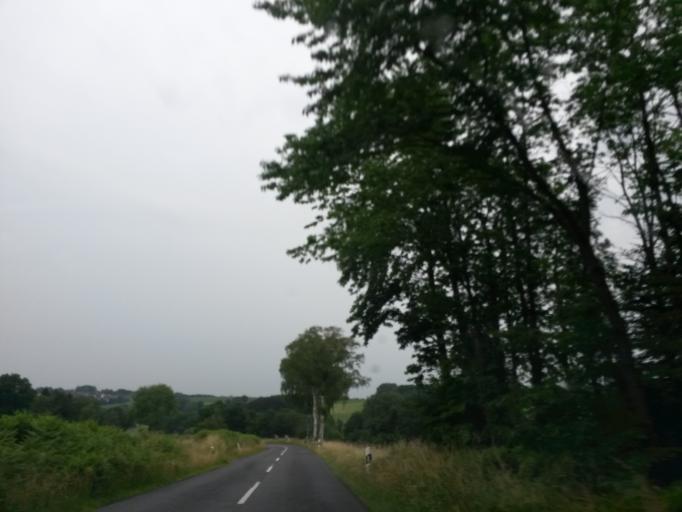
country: DE
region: North Rhine-Westphalia
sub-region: Regierungsbezirk Koln
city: Much
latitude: 50.9319
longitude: 7.3790
